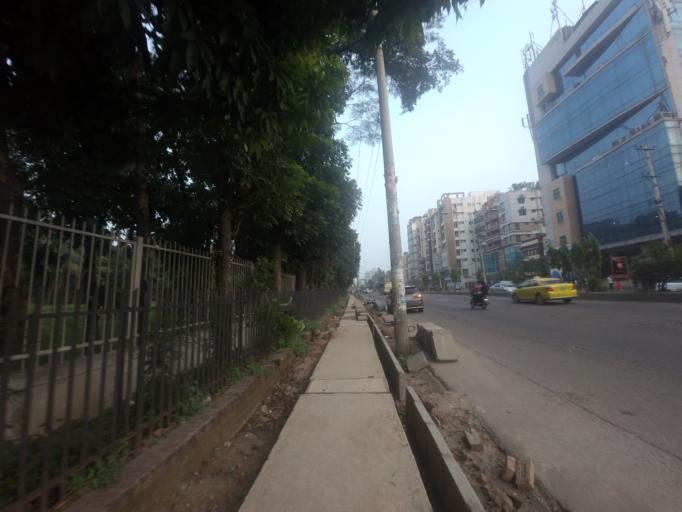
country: BD
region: Dhaka
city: Azimpur
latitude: 23.7634
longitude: 90.3713
